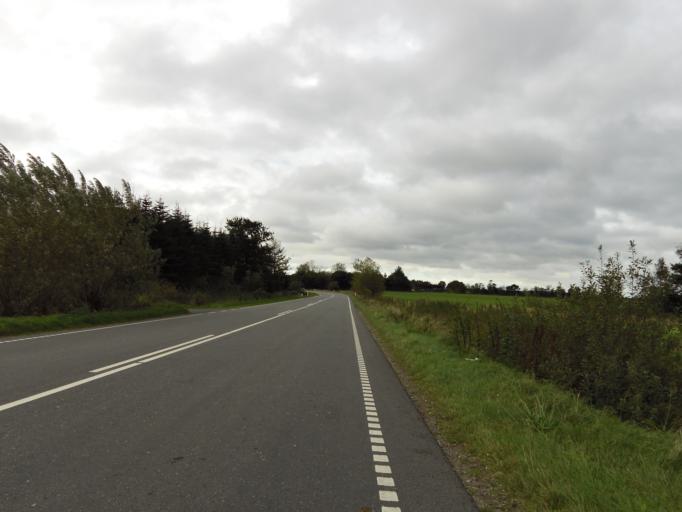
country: DK
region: South Denmark
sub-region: Tonder Kommune
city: Sherrebek
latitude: 55.2133
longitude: 8.8147
